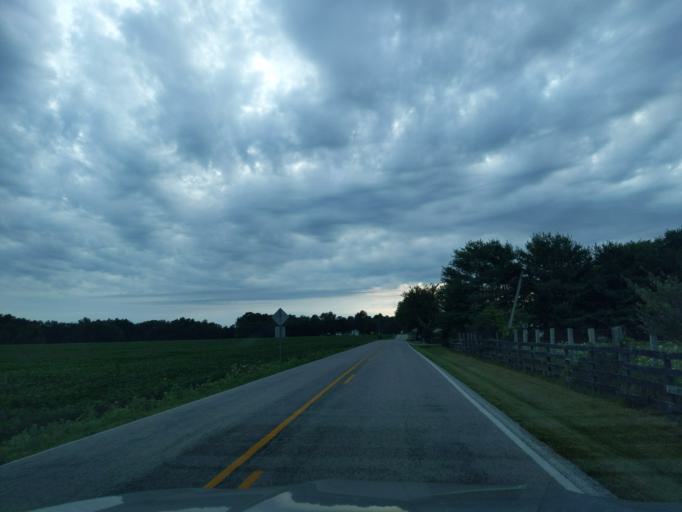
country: US
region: Indiana
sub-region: Ripley County
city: Sunman
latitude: 39.2023
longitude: -85.1759
